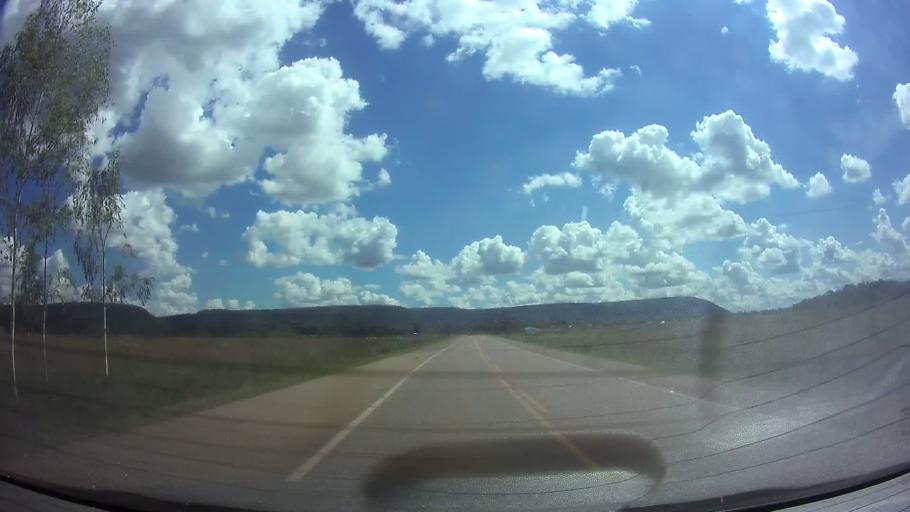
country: PY
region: Guaira
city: Itape
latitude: -25.9133
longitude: -56.6789
